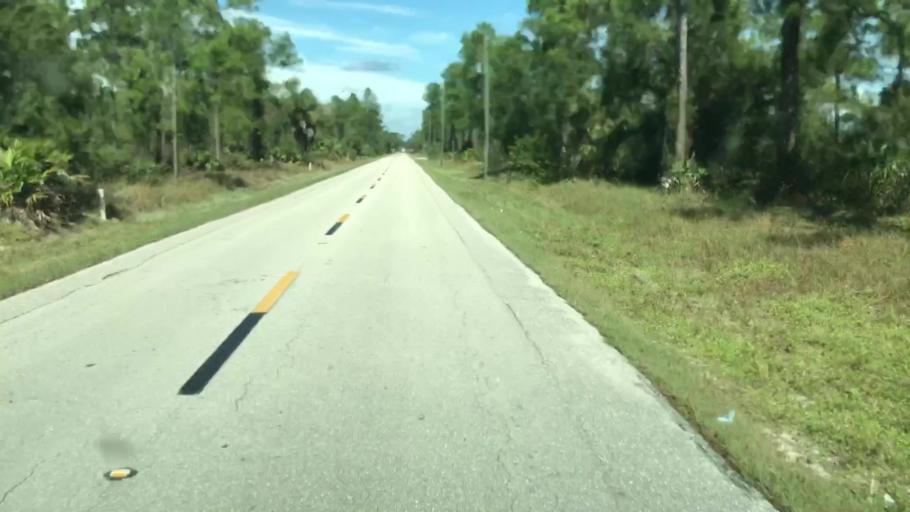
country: US
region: Florida
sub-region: Lee County
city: Lehigh Acres
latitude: 26.6452
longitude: -81.6465
